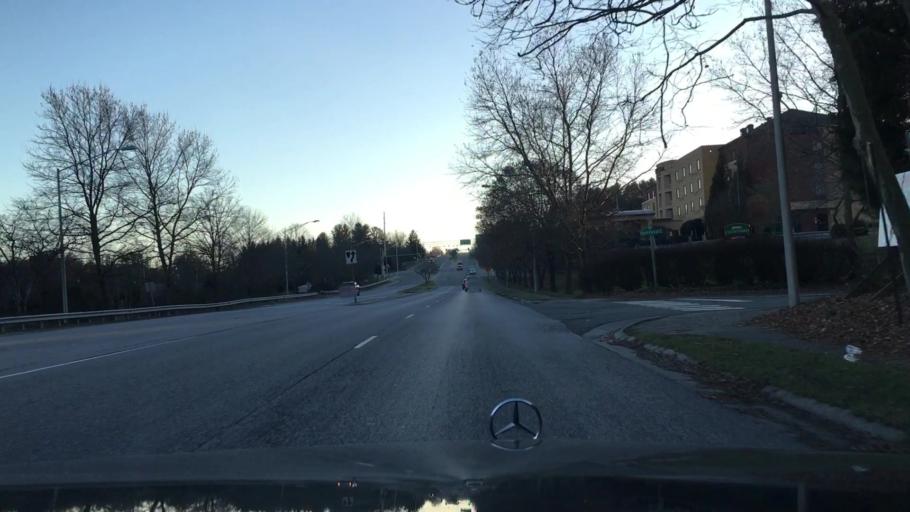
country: US
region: Virginia
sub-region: Montgomery County
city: Merrimac
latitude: 37.2002
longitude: -80.4004
